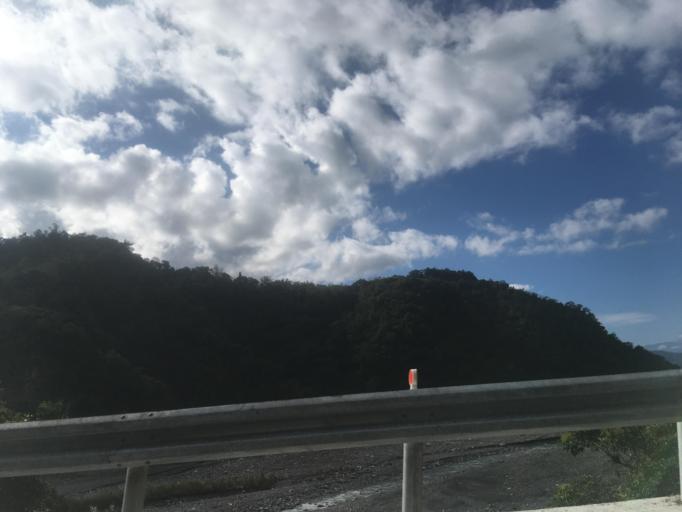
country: TW
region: Taiwan
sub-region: Yilan
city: Yilan
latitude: 24.6412
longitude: 121.5631
